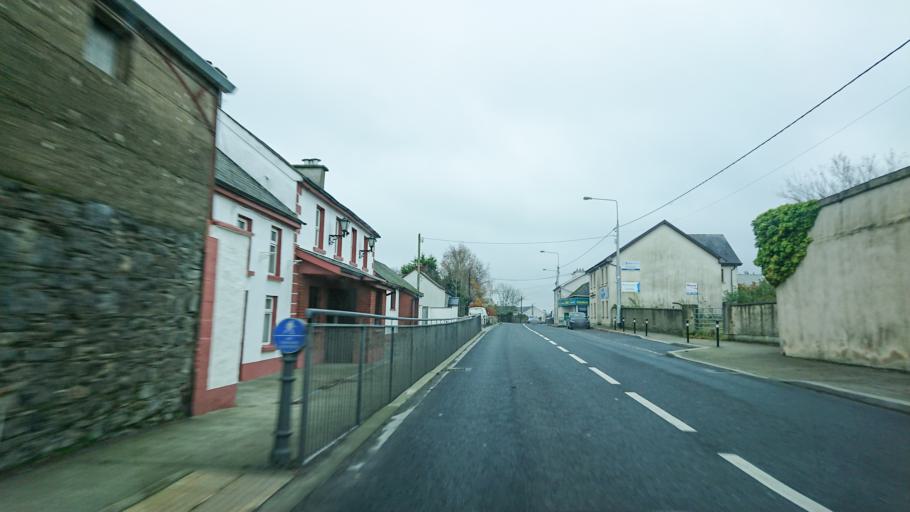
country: IE
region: Leinster
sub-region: Kilkenny
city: Mooncoin
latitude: 52.2944
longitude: -7.2571
